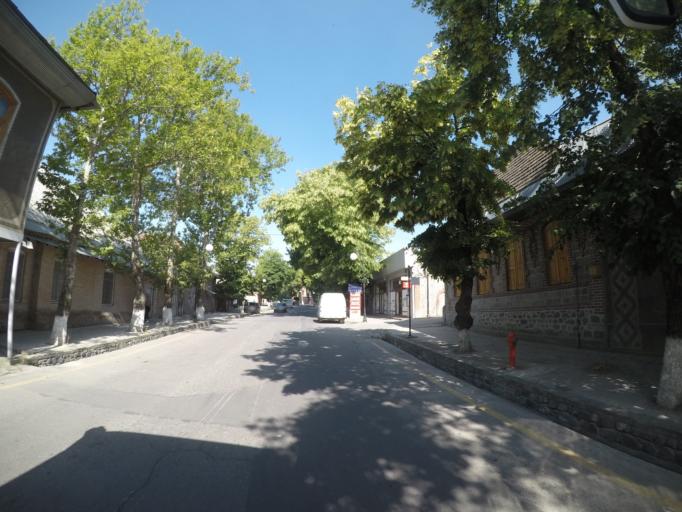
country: AZ
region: Shaki City
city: Sheki
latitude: 41.2056
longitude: 47.1761
